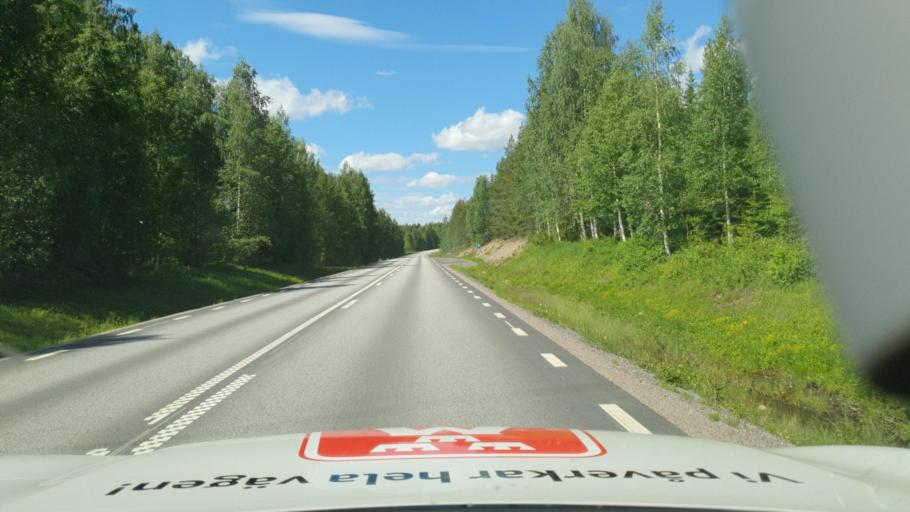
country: SE
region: Vaesterbotten
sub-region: Skelleftea Kommun
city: Boliden
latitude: 64.9015
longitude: 20.3644
